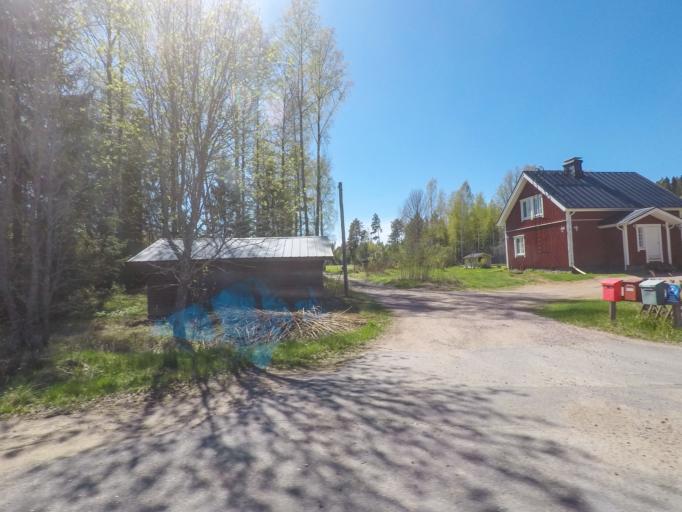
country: FI
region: Uusimaa
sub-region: Helsinki
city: Sammatti
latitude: 60.3344
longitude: 23.8019
